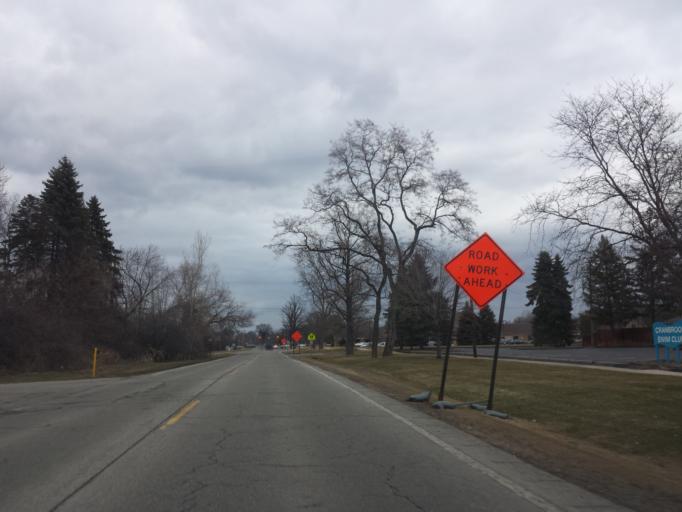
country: US
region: Michigan
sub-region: Oakland County
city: Beverly Hills
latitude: 42.5134
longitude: -83.2424
